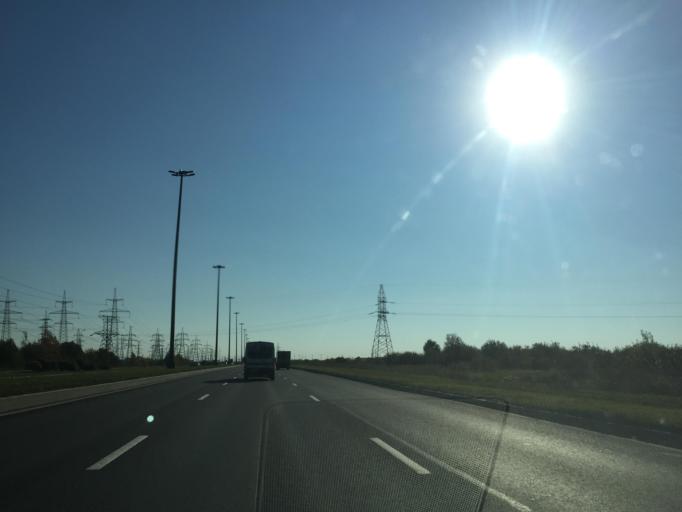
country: RU
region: St.-Petersburg
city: Petro-Slavyanka
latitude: 59.7598
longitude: 30.5129
